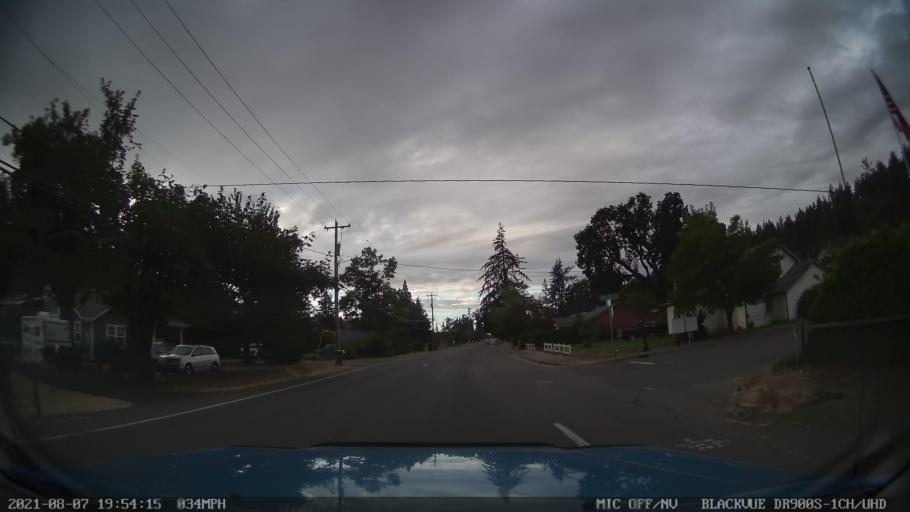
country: US
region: Oregon
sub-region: Marion County
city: Silverton
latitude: 44.9936
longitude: -122.7722
